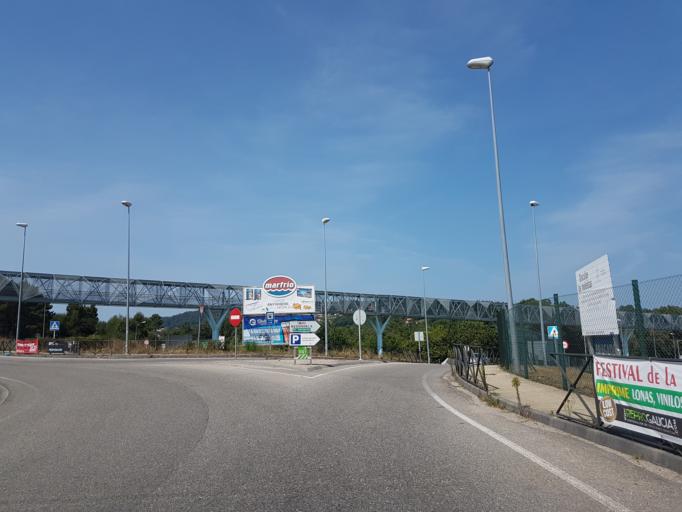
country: ES
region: Galicia
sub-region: Provincia de Pontevedra
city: Porrino
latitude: 42.2238
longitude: -8.6347
